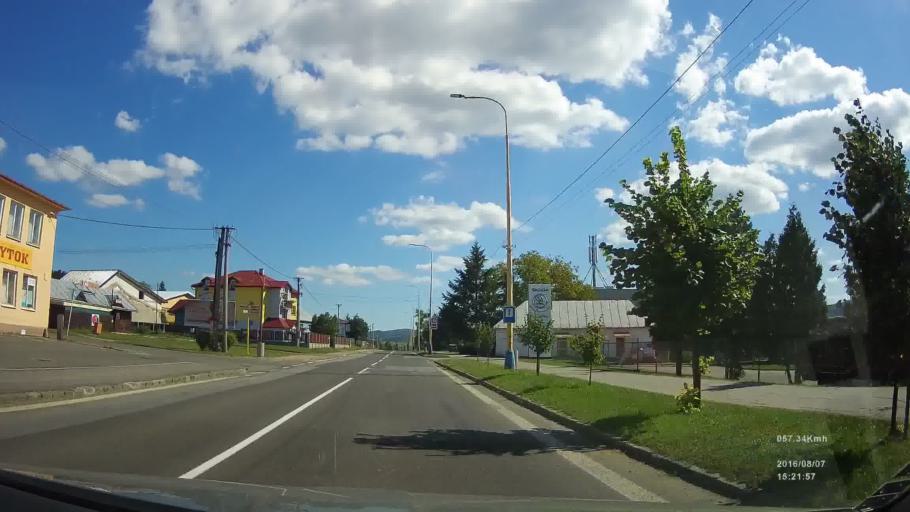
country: SK
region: Presovsky
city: Stropkov
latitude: 49.1965
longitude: 21.6535
